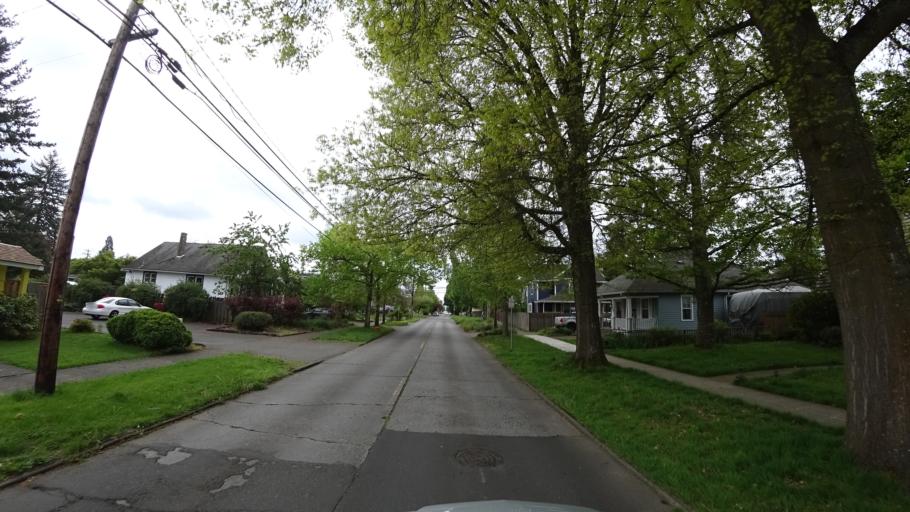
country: US
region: Oregon
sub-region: Washington County
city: Hillsboro
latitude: 45.5259
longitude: -122.9825
